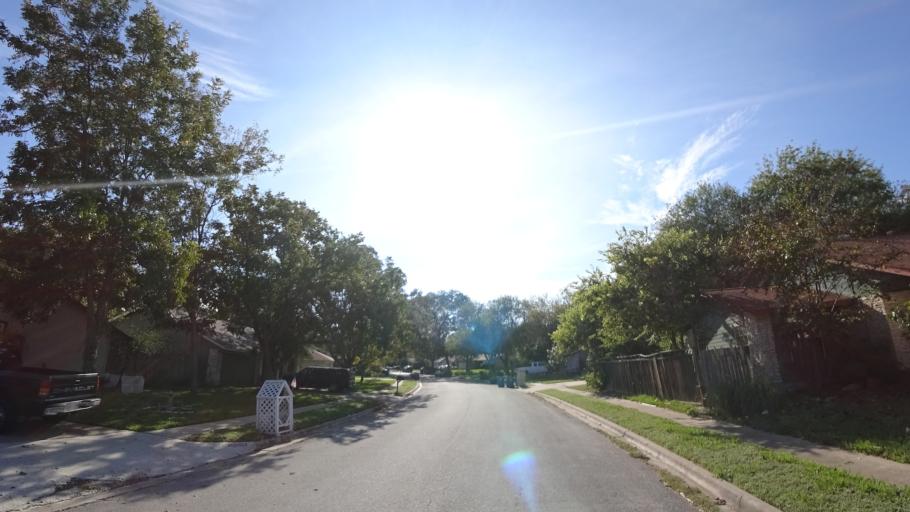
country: US
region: Texas
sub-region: Williamson County
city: Anderson Mill
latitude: 30.4558
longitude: -97.8005
